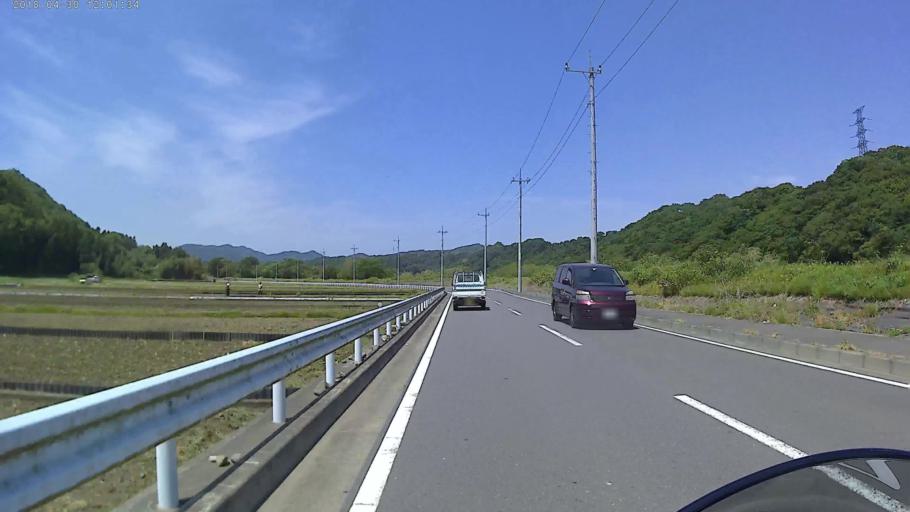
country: JP
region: Kanagawa
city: Zama
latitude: 35.5182
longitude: 139.3247
